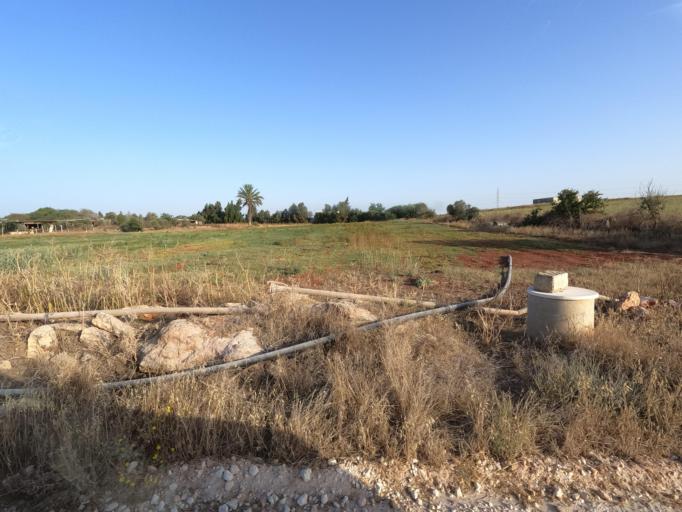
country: CY
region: Ammochostos
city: Liopetri
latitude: 34.9945
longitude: 33.8851
